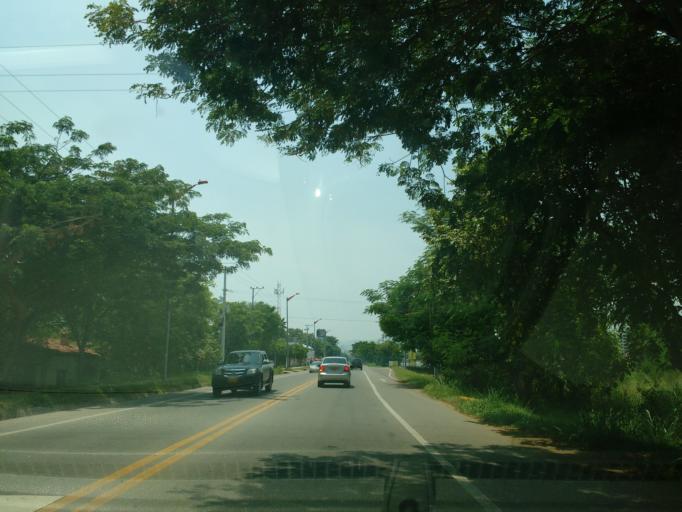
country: CO
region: Cundinamarca
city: Ricaurte
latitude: 4.2859
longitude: -74.7744
